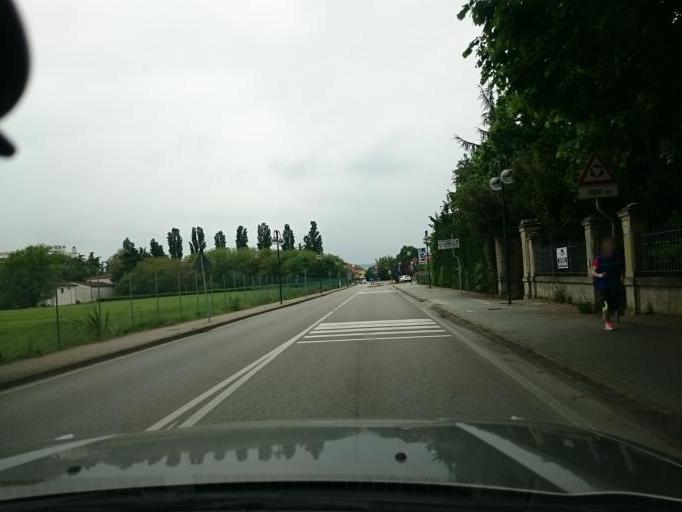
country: IT
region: Veneto
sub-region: Provincia di Padova
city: Montegrotto Terme
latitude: 45.3247
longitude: 11.8044
